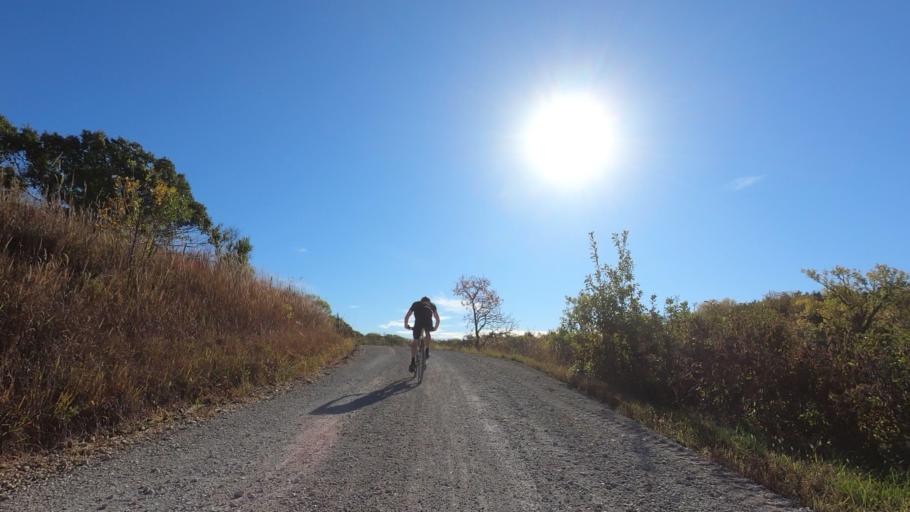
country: US
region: Kansas
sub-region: Pottawatomie County
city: Westmoreland
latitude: 39.4820
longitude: -96.5947
